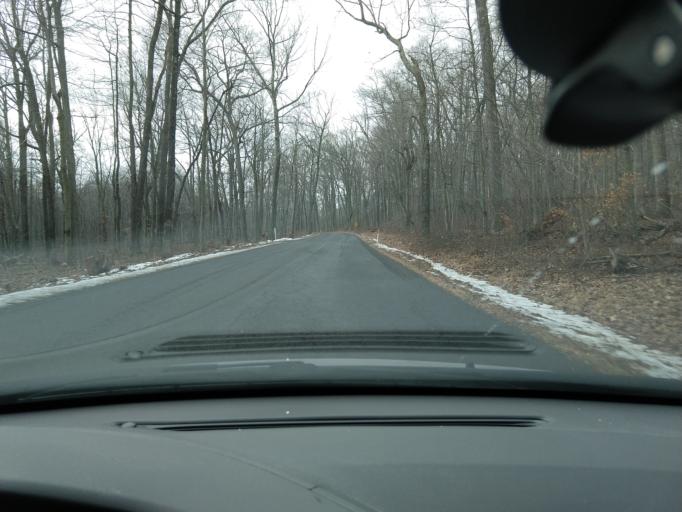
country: US
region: Pennsylvania
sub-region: Berks County
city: Birdsboro
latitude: 40.2098
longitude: -75.7746
